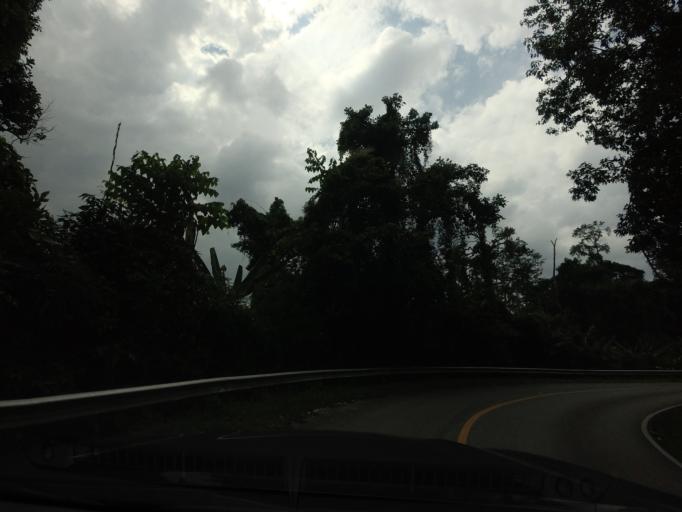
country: TH
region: Loei
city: Na Haeo
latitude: 17.7062
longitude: 100.9489
